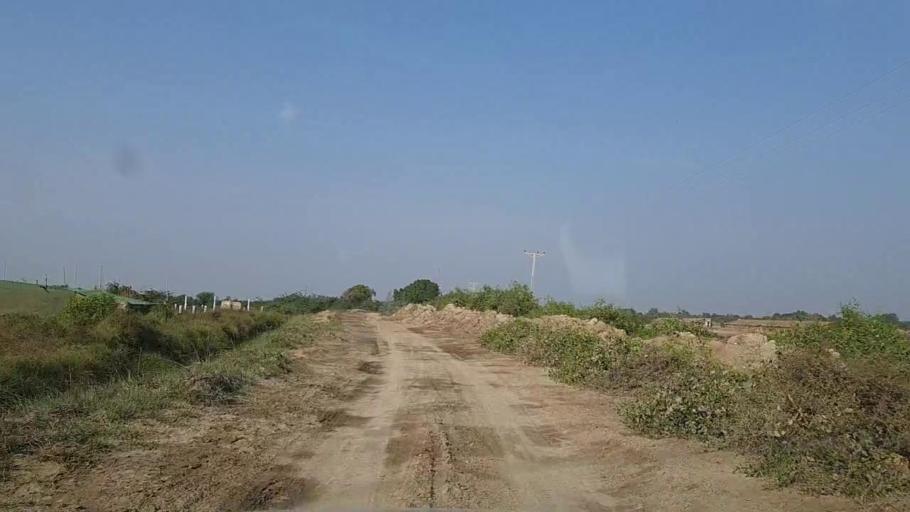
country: PK
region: Sindh
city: Mirpur Sakro
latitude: 24.5838
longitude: 67.5678
